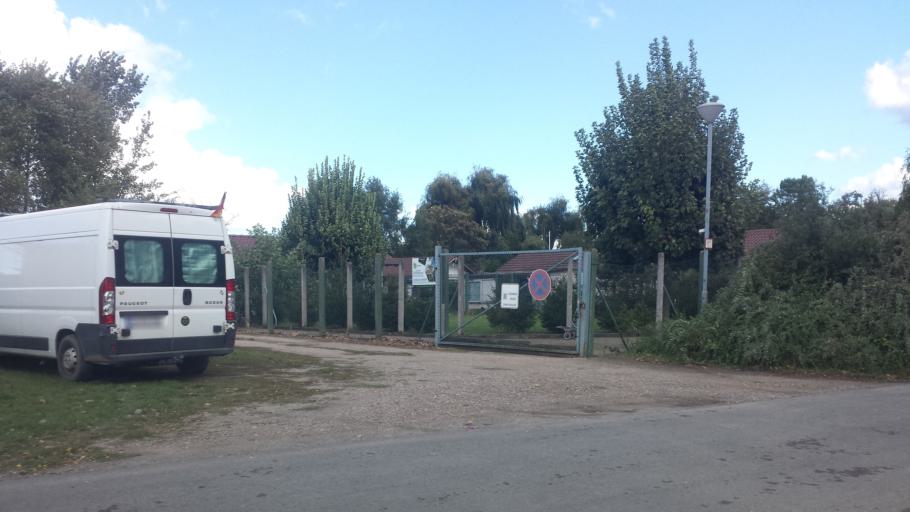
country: DE
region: Rheinland-Pfalz
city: Bobenheim-Roxheim
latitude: 49.5884
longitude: 8.3702
